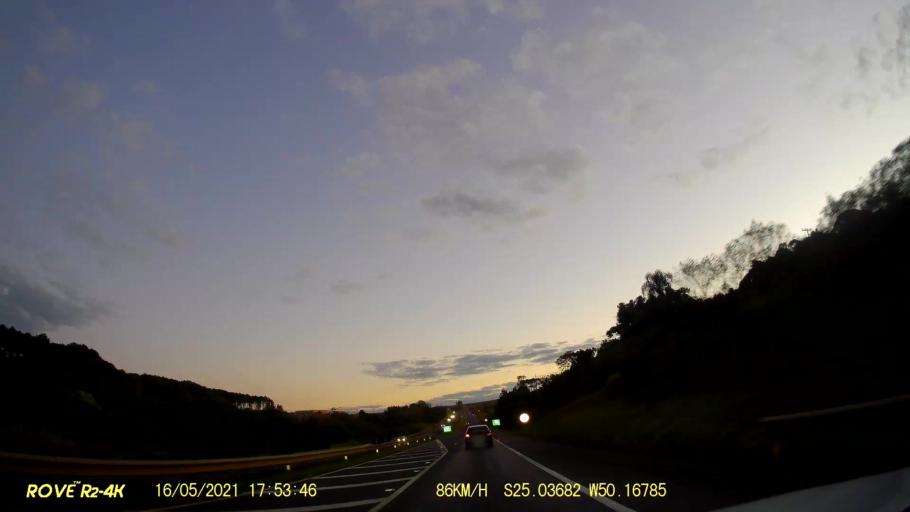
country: BR
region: Parana
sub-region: Ponta Grossa
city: Ponta Grossa
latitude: -25.0368
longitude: -50.1678
